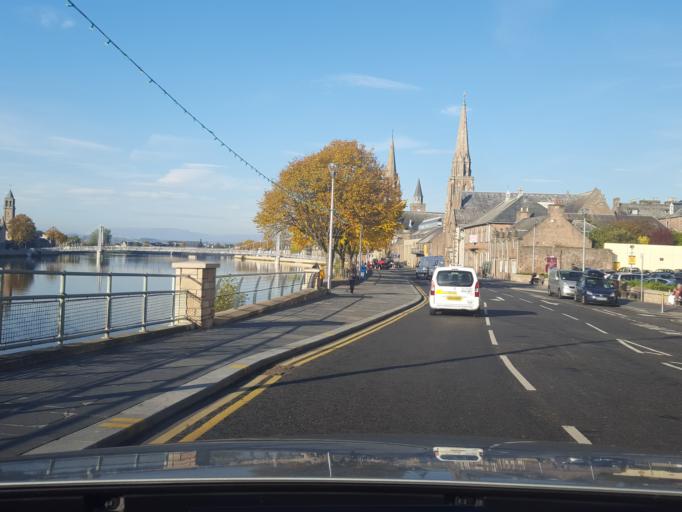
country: GB
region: Scotland
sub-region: Highland
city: Inverness
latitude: 57.4774
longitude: -4.2271
